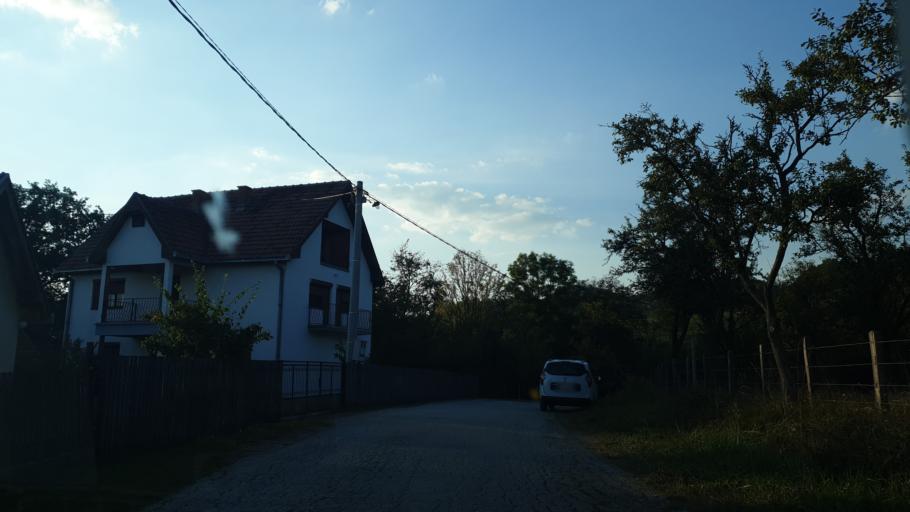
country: RS
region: Central Serbia
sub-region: Zlatiborski Okrug
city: Kosjeric
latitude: 43.9926
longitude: 20.0026
